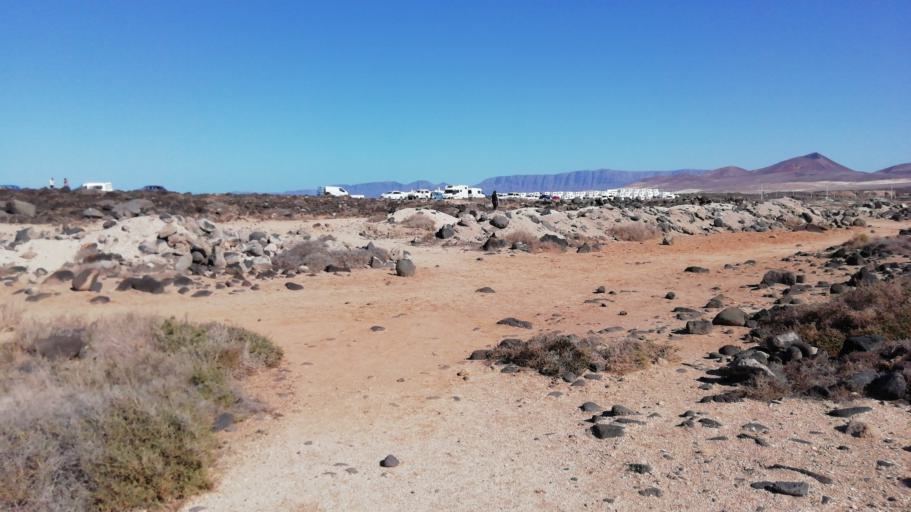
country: ES
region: Canary Islands
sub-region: Provincia de Las Palmas
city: Tinajo
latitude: 29.1162
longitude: -13.6611
